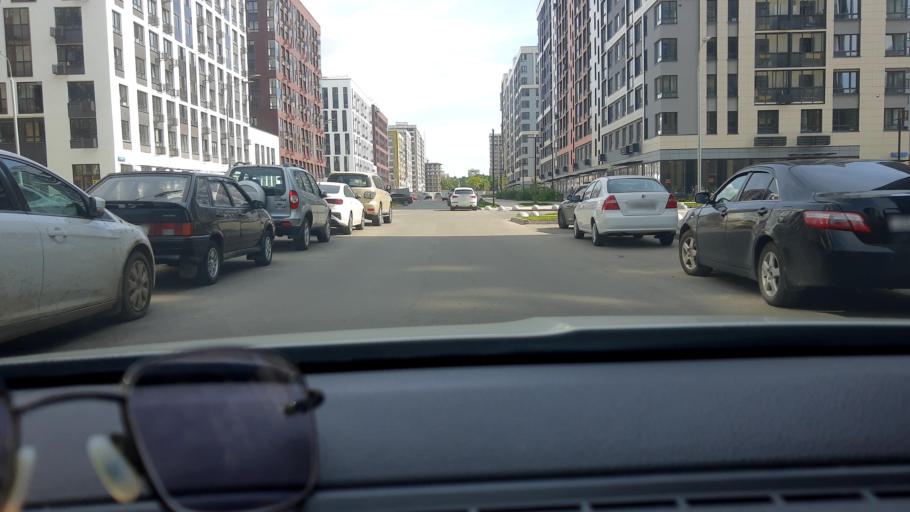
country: RU
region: Moskovskaya
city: Kommunarka
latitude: 55.5670
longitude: 37.4973
